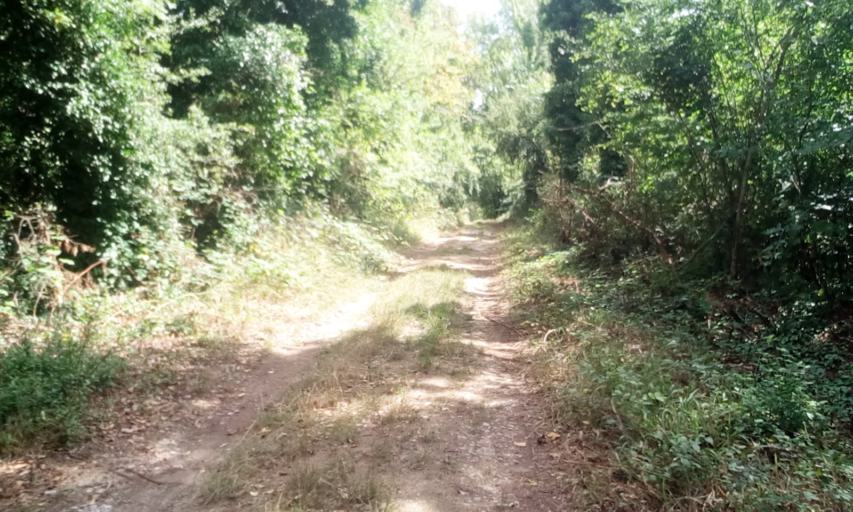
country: FR
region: Lower Normandy
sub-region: Departement du Calvados
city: Cagny
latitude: 49.1136
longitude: -0.2536
